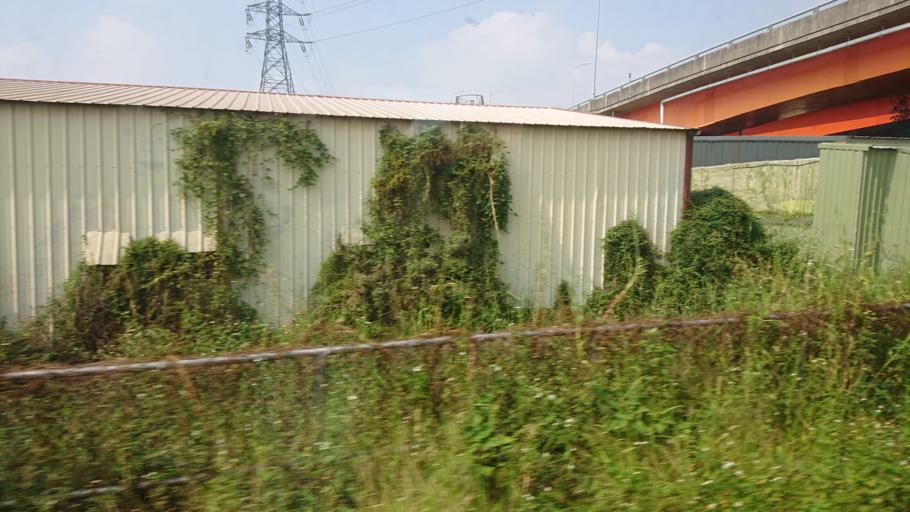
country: TW
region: Taiwan
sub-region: Yunlin
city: Douliu
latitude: 23.6566
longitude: 120.4737
